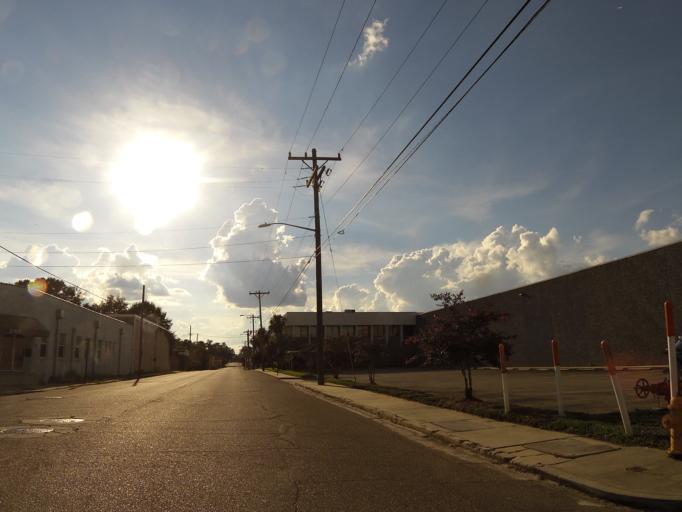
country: US
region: Florida
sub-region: Duval County
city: Jacksonville
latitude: 30.3300
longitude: -81.6833
